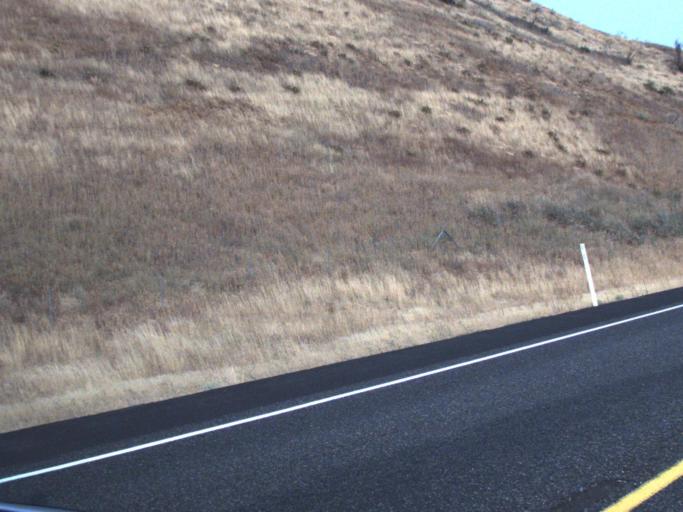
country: US
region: Washington
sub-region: Kittitas County
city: Ellensburg
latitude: 47.0917
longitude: -120.6548
